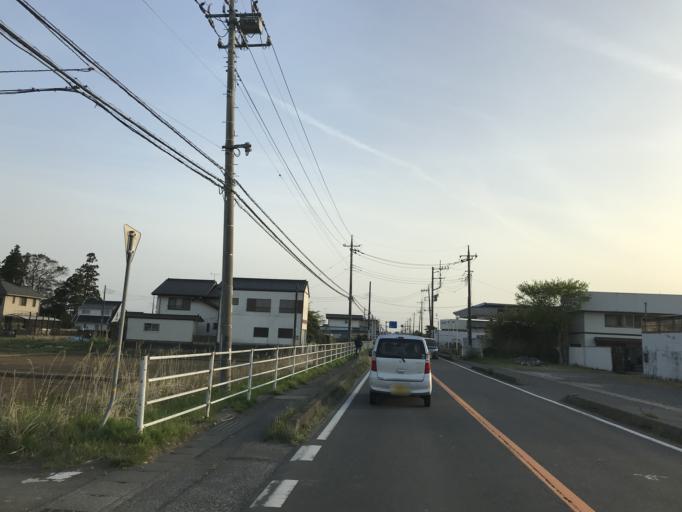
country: JP
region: Ibaraki
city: Katsuta
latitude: 36.3761
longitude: 140.5221
